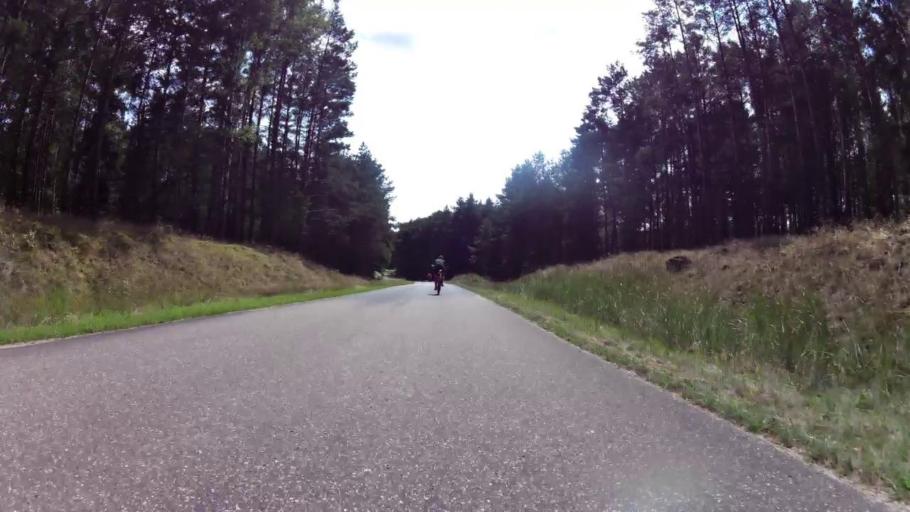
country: PL
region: West Pomeranian Voivodeship
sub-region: Powiat choszczenski
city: Drawno
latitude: 53.3591
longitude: 15.7056
